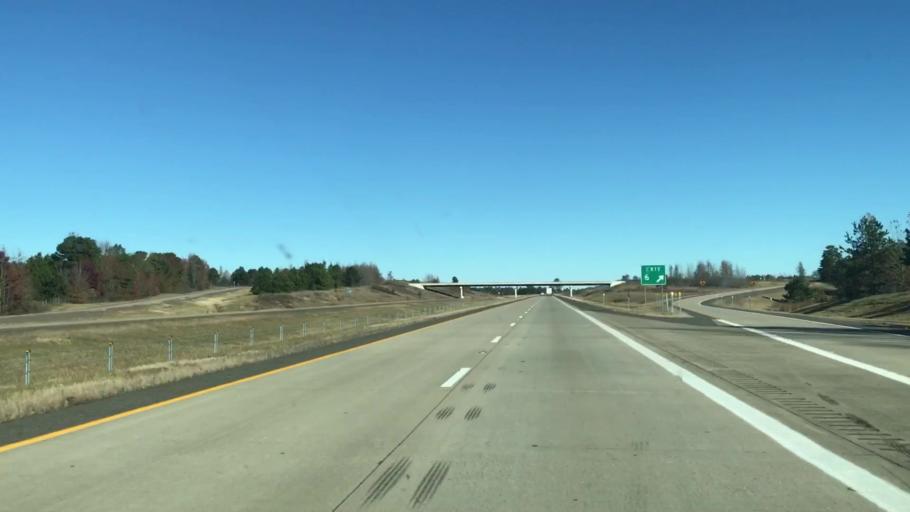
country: US
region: Texas
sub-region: Cass County
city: Queen City
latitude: 33.1161
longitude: -93.8938
